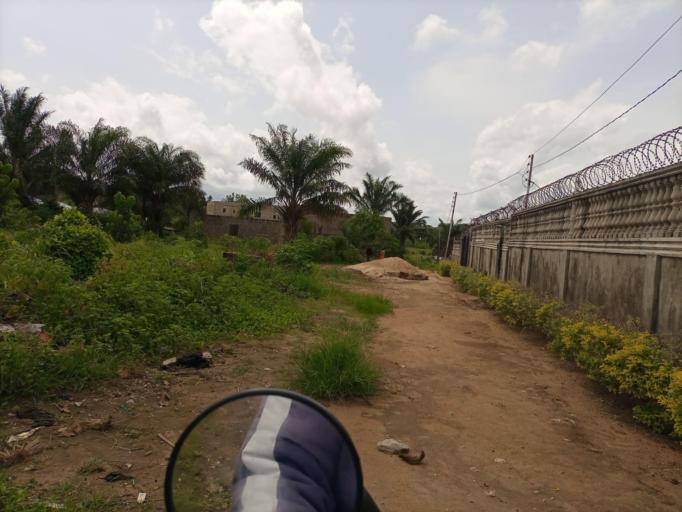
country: SL
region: Southern Province
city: Bo
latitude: 7.9715
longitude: -11.7676
